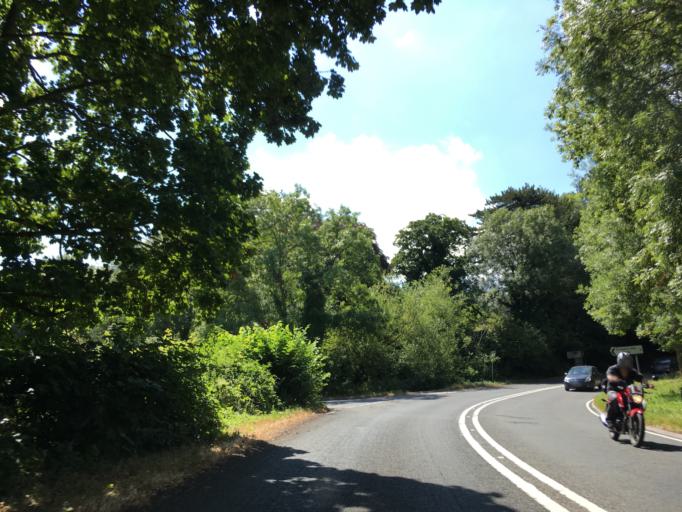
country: GB
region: England
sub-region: Gloucestershire
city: Churchdown
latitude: 51.8313
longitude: -2.1653
